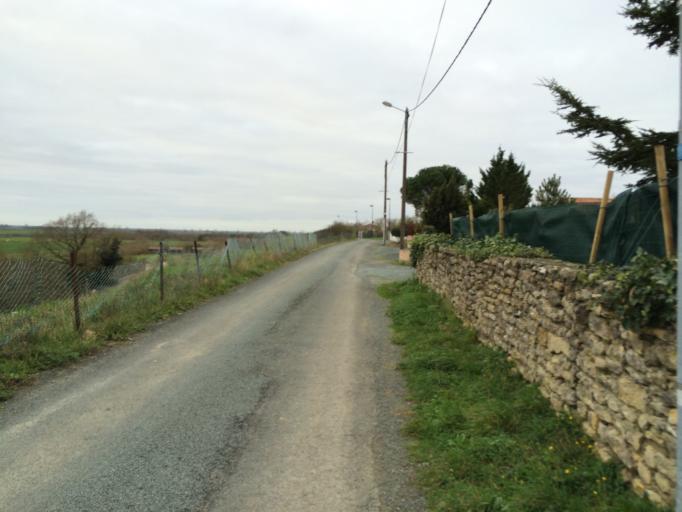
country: FR
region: Pays de la Loire
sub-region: Departement de la Vendee
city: Chaille-les-Marais
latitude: 46.3896
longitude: -1.0143
